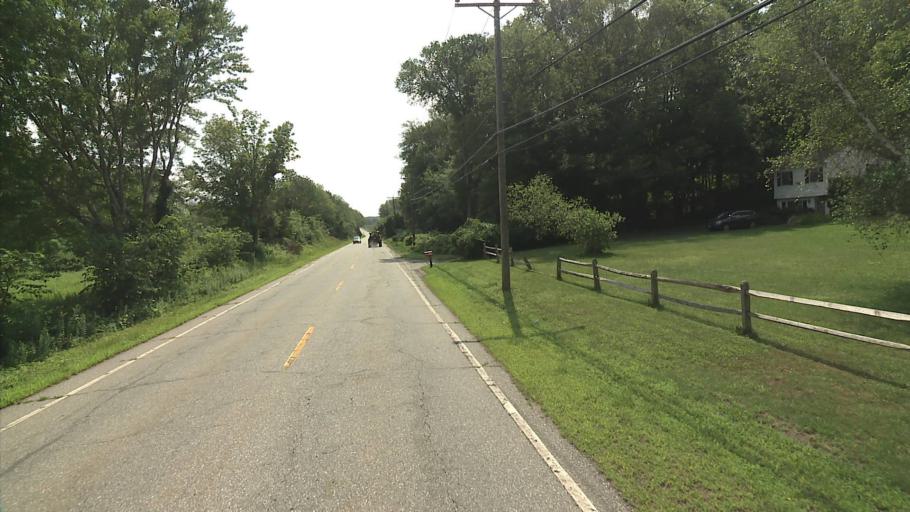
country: US
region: Connecticut
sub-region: New London County
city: Preston City
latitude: 41.5312
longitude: -71.9973
